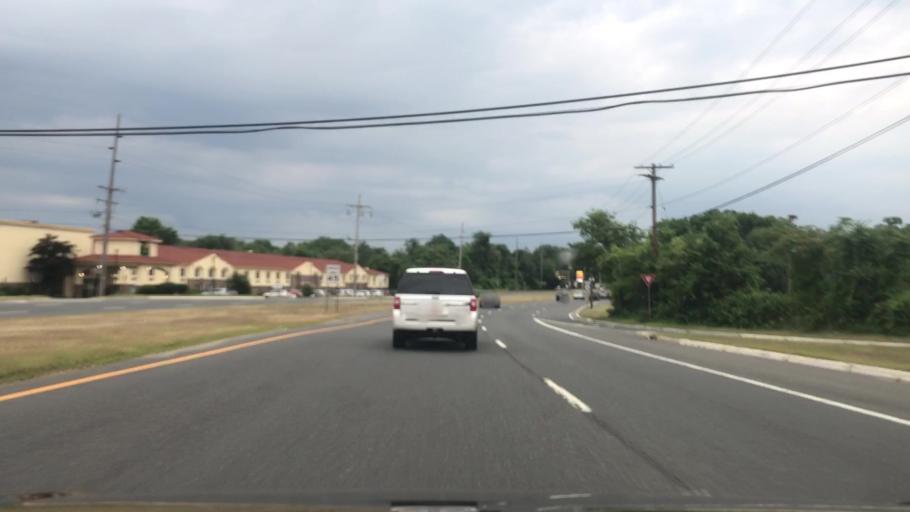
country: US
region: New Jersey
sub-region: Monmouth County
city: West Long Branch
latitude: 40.3001
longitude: -74.0212
